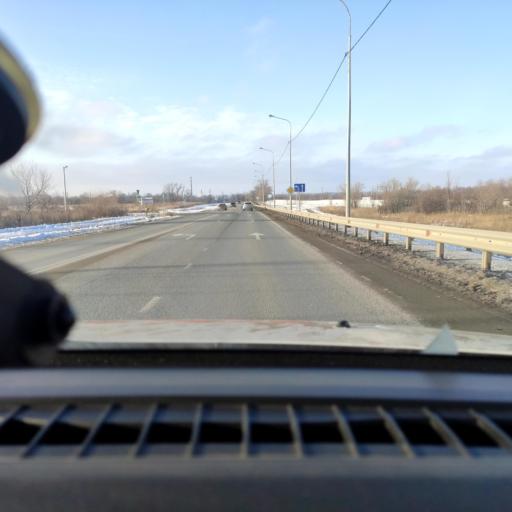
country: RU
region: Samara
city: Chapayevsk
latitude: 52.9968
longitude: 49.7359
